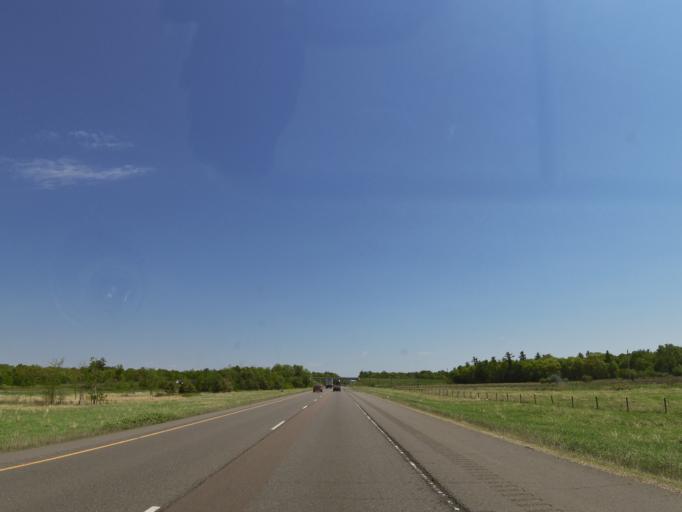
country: US
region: Wisconsin
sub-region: Monroe County
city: Tomah
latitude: 43.9550
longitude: -90.3526
